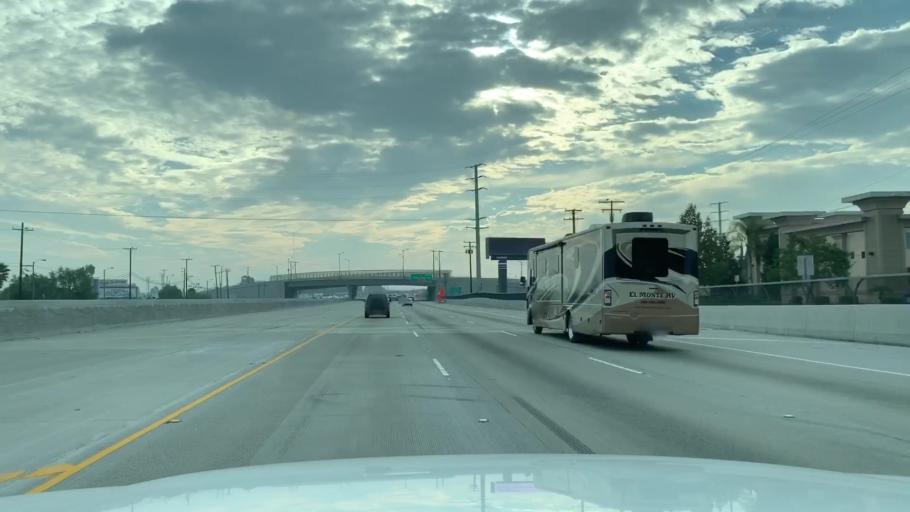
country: US
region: California
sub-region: Los Angeles County
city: La Mirada
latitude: 33.8894
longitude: -118.0391
